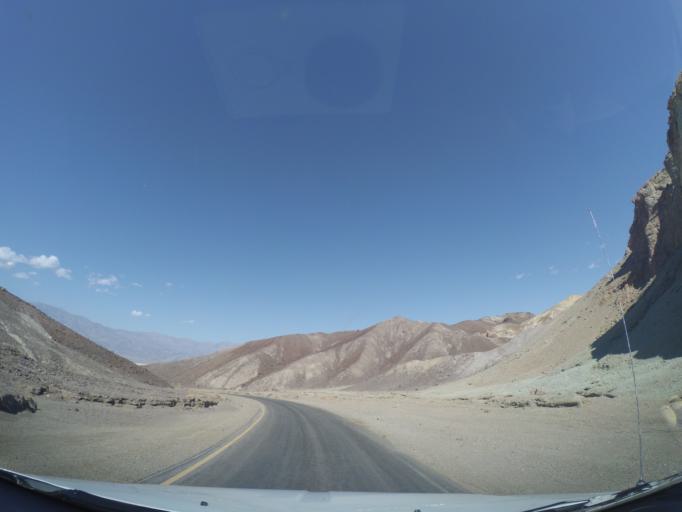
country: US
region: Nevada
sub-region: Nye County
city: Beatty
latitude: 36.3834
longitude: -116.8320
